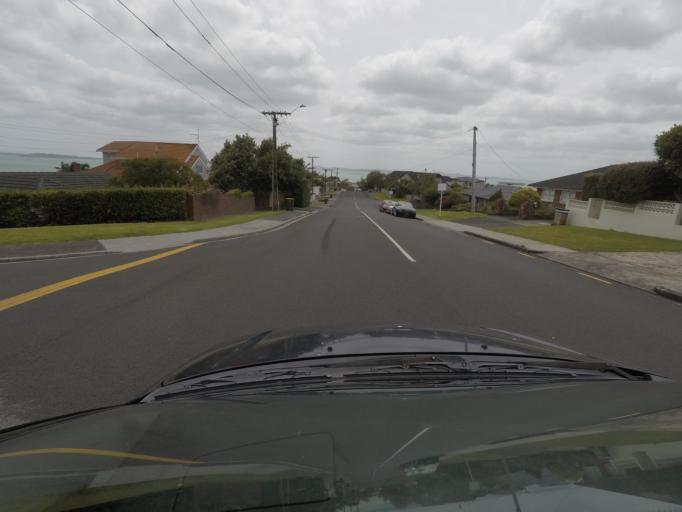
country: NZ
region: Auckland
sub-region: Auckland
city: Pakuranga
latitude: -36.8893
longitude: 174.9311
